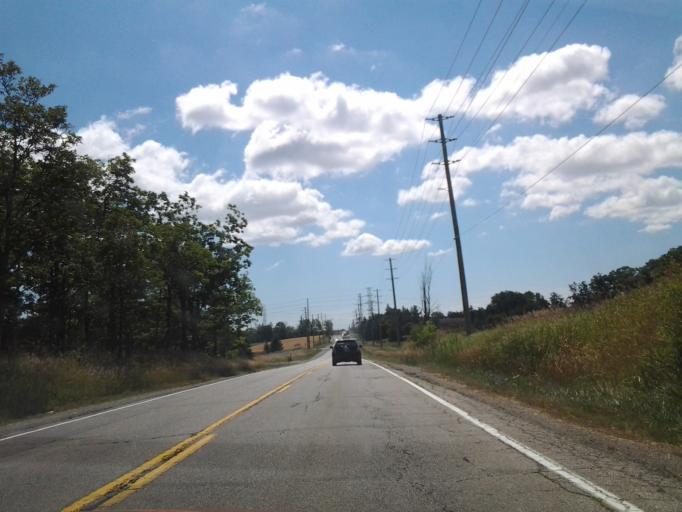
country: CA
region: Ontario
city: Burlington
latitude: 43.4363
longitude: -79.8131
